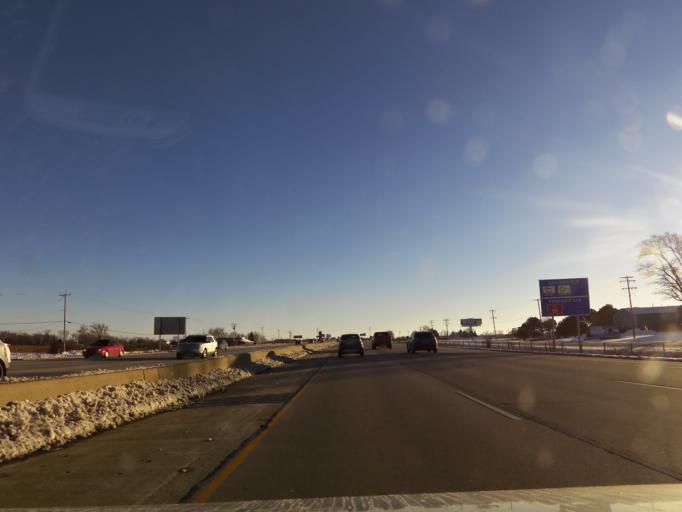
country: US
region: Wisconsin
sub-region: Racine County
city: Sturtevant
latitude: 42.7039
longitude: -87.9539
